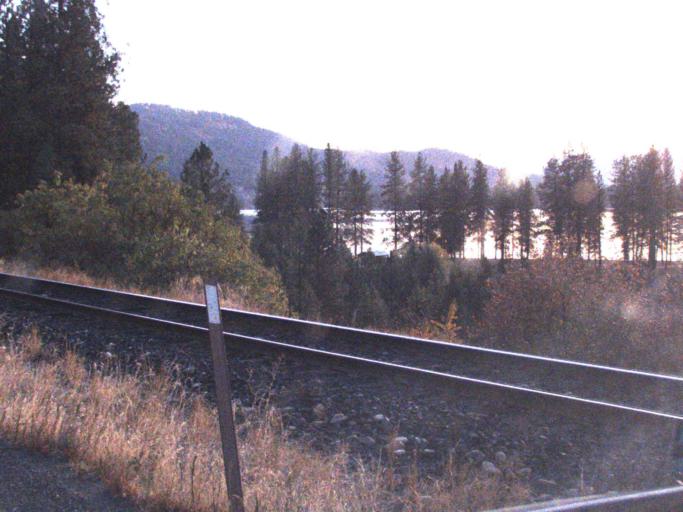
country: US
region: Washington
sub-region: Stevens County
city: Kettle Falls
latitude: 48.6985
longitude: -118.0140
